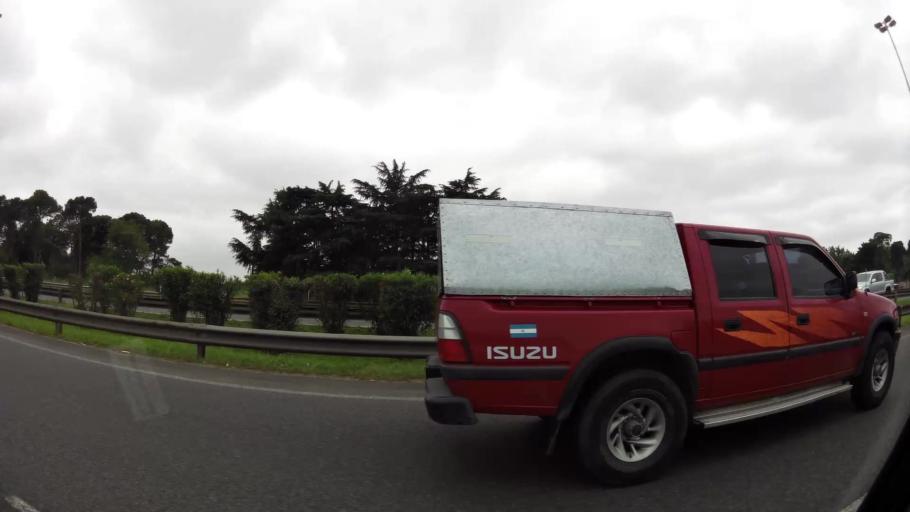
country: AR
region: Buenos Aires
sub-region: Partido de Ezeiza
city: Ezeiza
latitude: -34.8010
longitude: -58.5135
